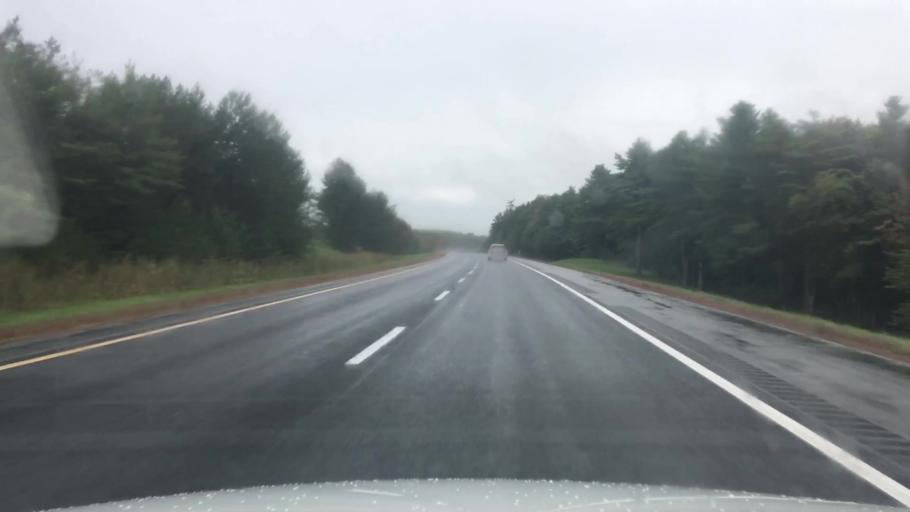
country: US
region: Maine
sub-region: Sagadahoc County
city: Topsham
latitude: 43.9863
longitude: -69.9409
